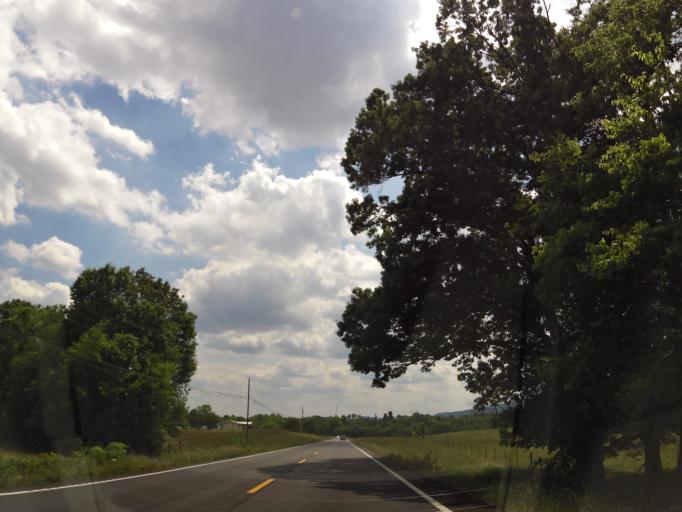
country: US
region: Tennessee
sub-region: Sequatchie County
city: Dunlap
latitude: 35.4674
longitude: -85.3227
